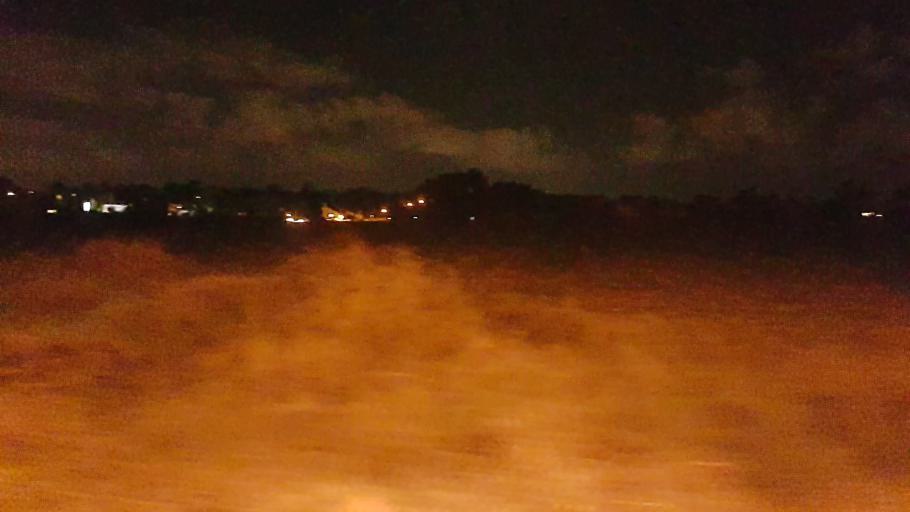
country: IL
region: Central District
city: Hod HaSharon
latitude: 32.1655
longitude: 34.8898
